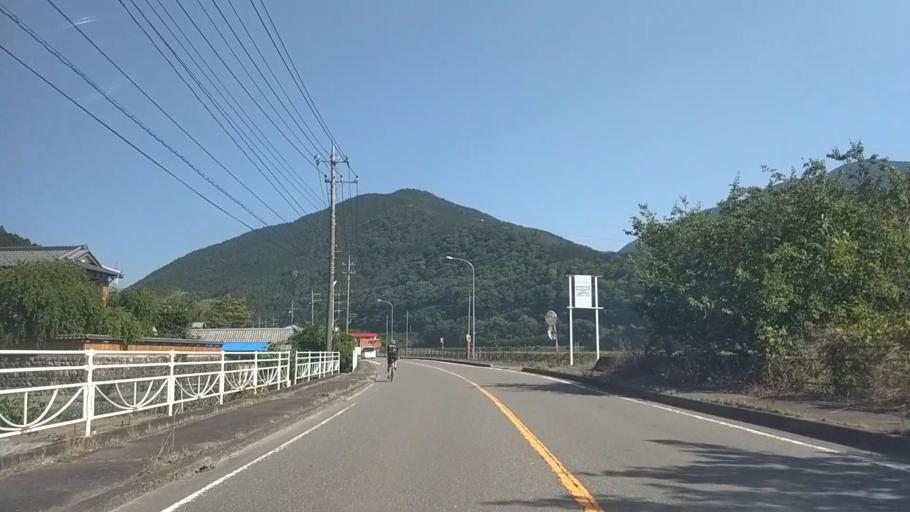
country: JP
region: Shizuoka
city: Fujinomiya
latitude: 35.2348
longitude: 138.5065
